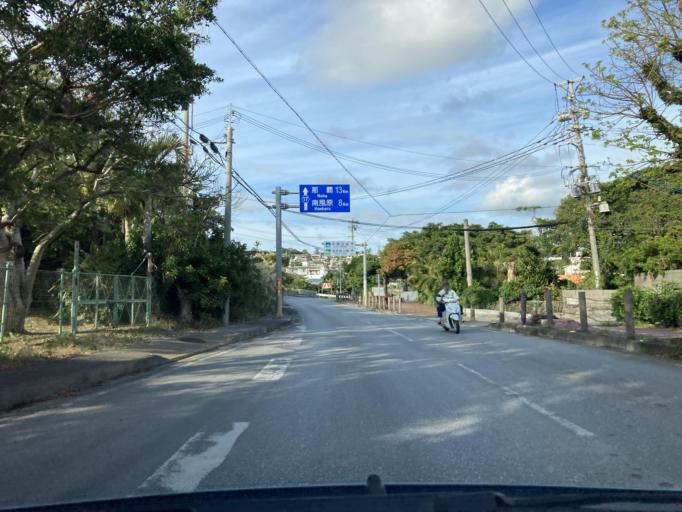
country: JP
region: Okinawa
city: Tomigusuku
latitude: 26.1414
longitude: 127.7477
